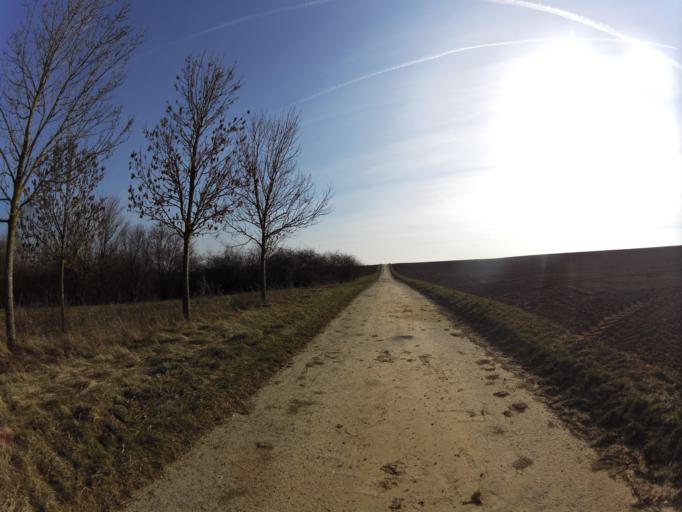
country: DE
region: Bavaria
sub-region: Regierungsbezirk Unterfranken
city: Prosselsheim
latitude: 49.8307
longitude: 10.1336
